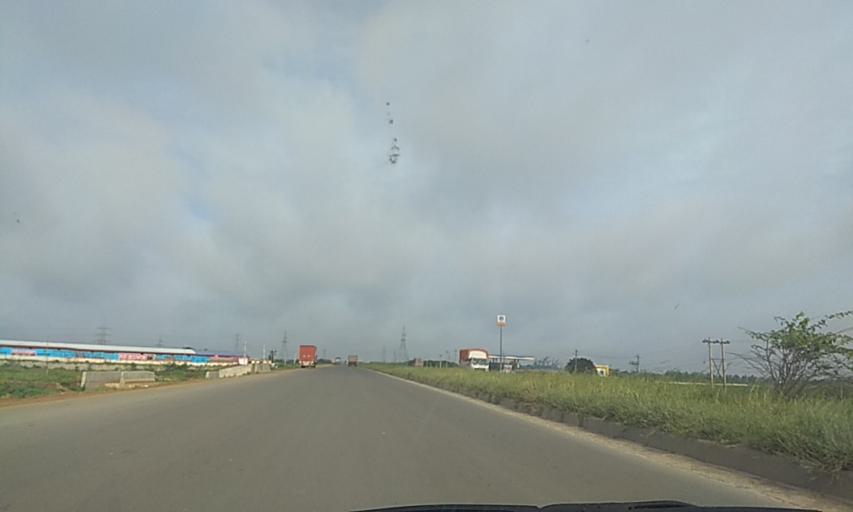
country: IN
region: Karnataka
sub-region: Haveri
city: Haveri
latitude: 14.7758
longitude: 75.3999
